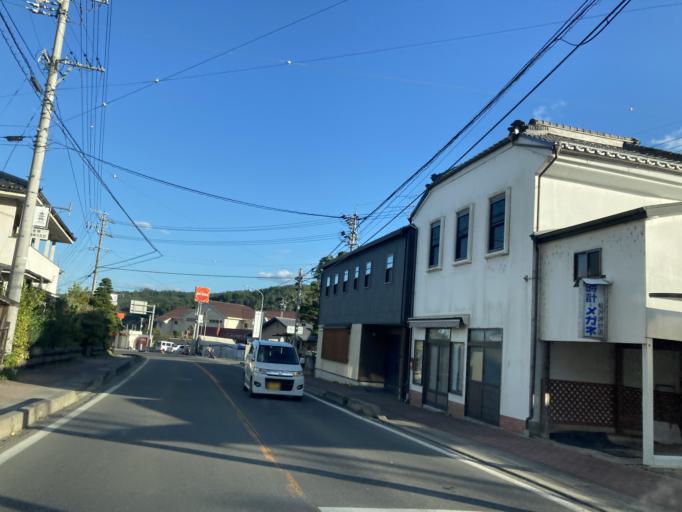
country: JP
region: Nagano
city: Kamimaruko
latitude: 36.3698
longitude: 138.1268
